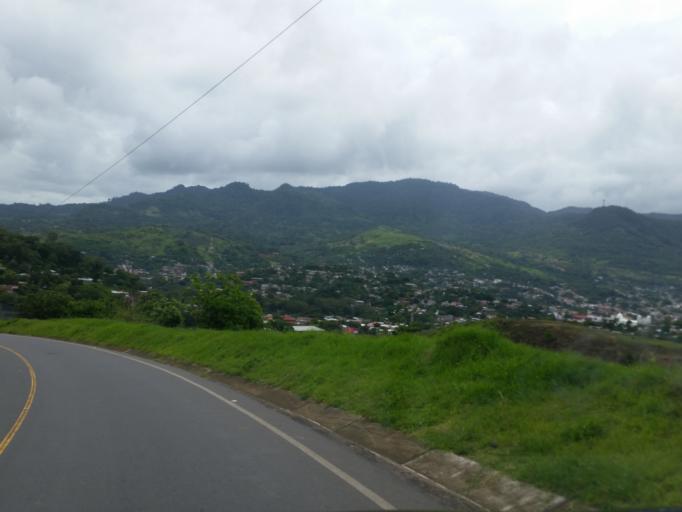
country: NI
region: Matagalpa
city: Matagalpa
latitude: 12.9408
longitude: -85.9239
